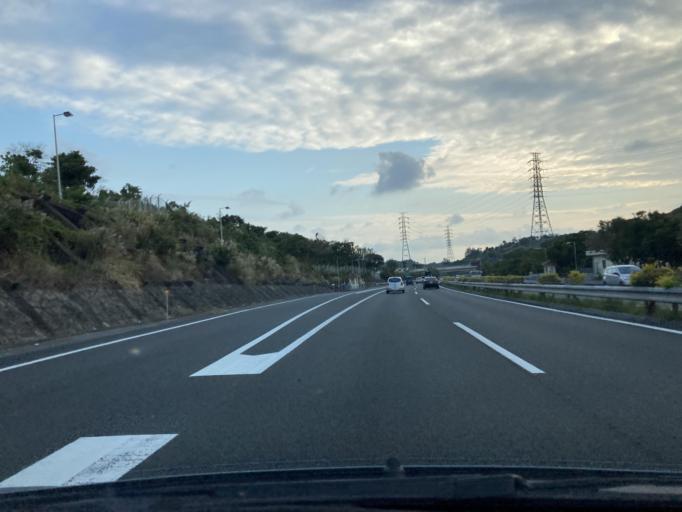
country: JP
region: Okinawa
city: Okinawa
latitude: 26.3186
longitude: 127.7896
